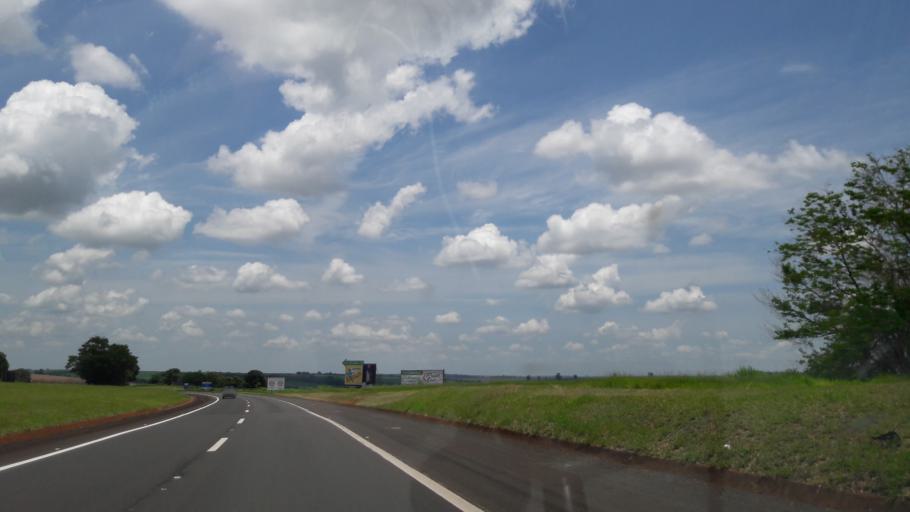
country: BR
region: Sao Paulo
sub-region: Avare
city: Avare
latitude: -22.9554
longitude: -48.8218
